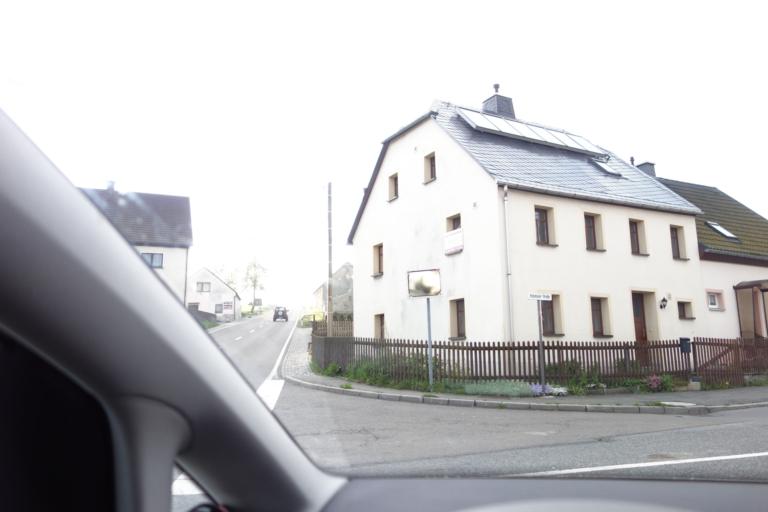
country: DE
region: Saxony
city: Zoblitz
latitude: 50.6471
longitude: 13.2577
